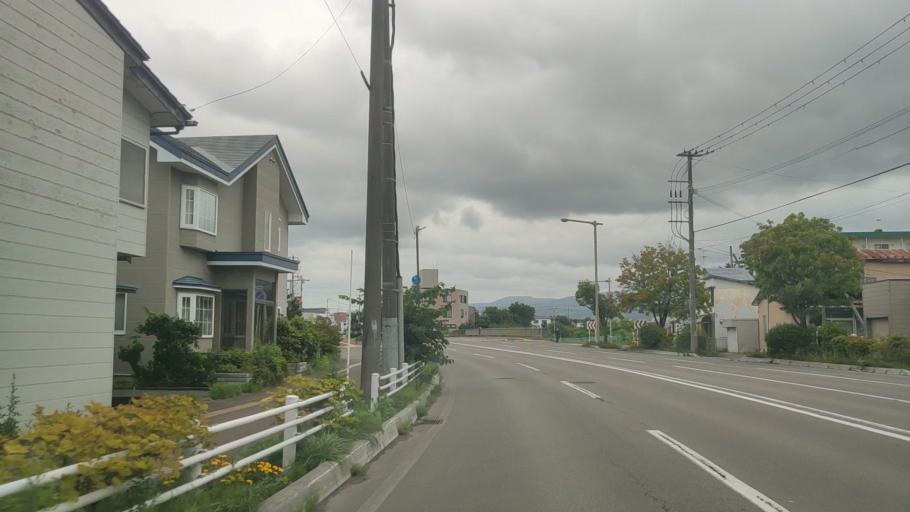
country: JP
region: Hokkaido
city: Hakodate
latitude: 41.7976
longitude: 140.7511
